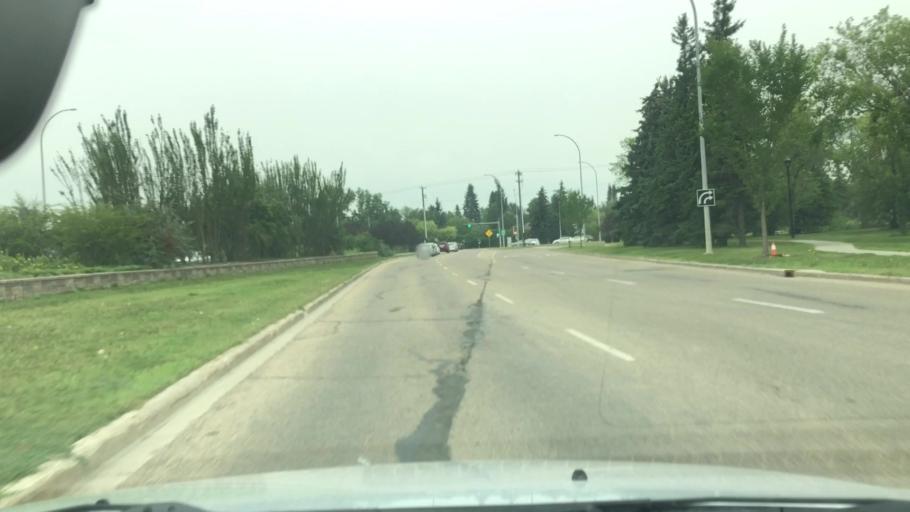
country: CA
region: Alberta
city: Edmonton
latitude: 53.4966
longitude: -113.5166
